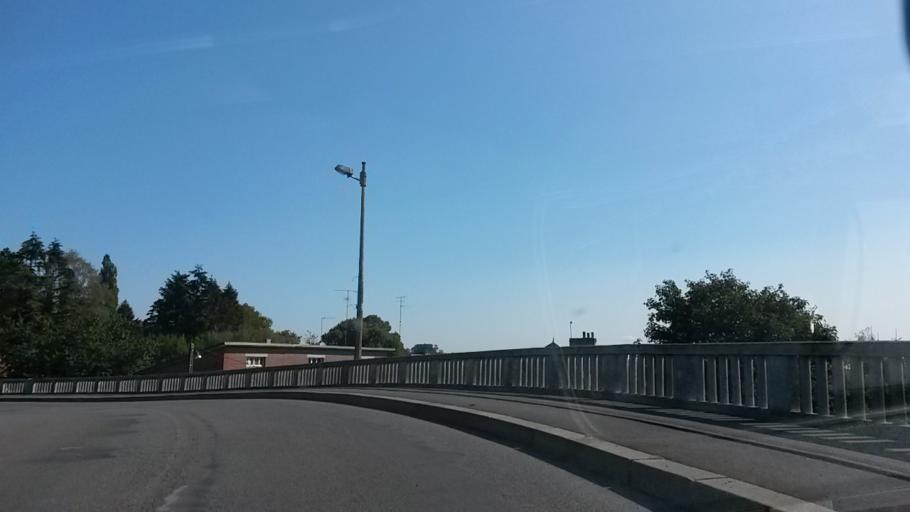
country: FR
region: Nord-Pas-de-Calais
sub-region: Departement du Nord
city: Avesnes-sur-Helpe
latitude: 50.1253
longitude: 3.9357
